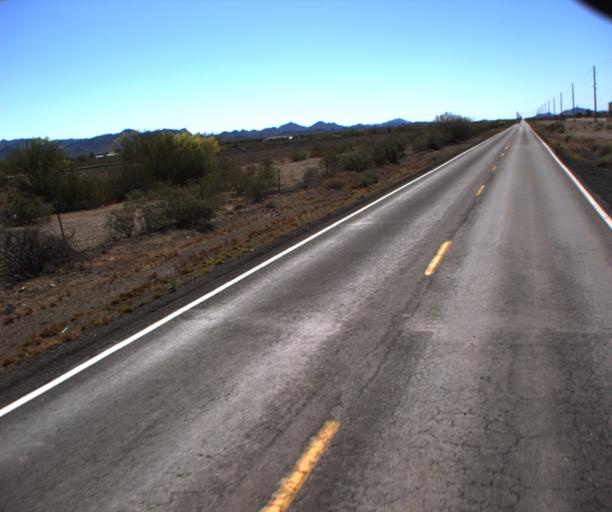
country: US
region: Arizona
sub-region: La Paz County
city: Salome
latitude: 33.8074
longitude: -113.8438
